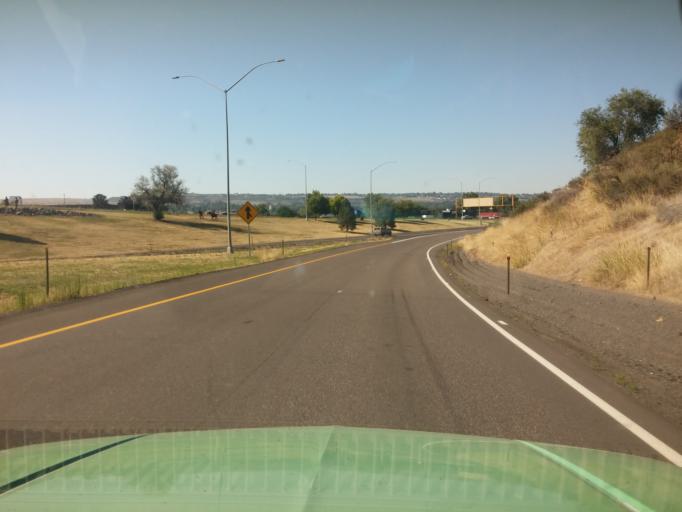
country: US
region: Idaho
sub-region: Nez Perce County
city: Lewiston
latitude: 46.4302
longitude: -116.9958
